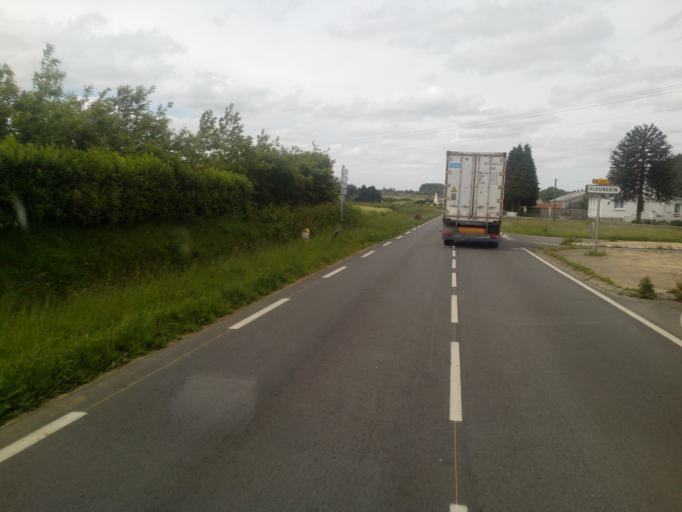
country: FR
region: Brittany
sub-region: Departement du Finistere
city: Guerlesquin
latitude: 48.5346
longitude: -3.5978
